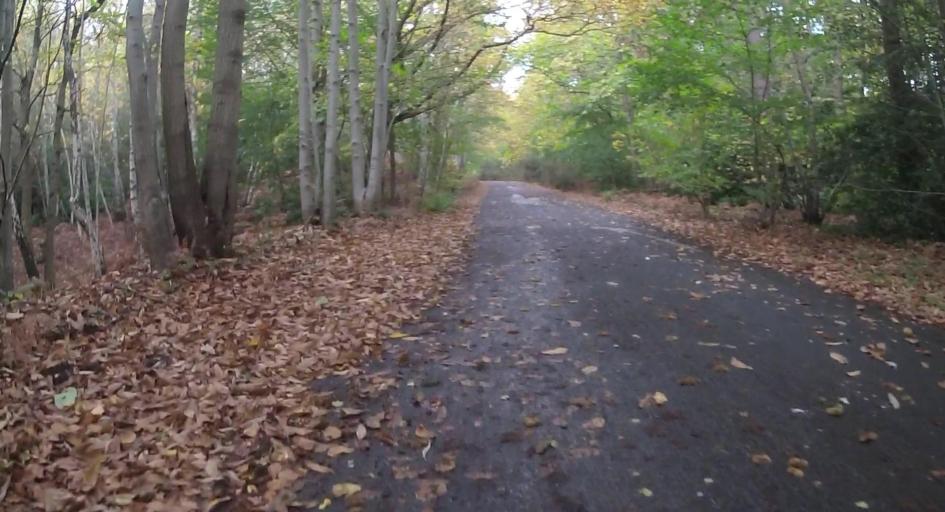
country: GB
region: England
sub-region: Surrey
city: Frimley
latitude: 51.3058
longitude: -0.7109
